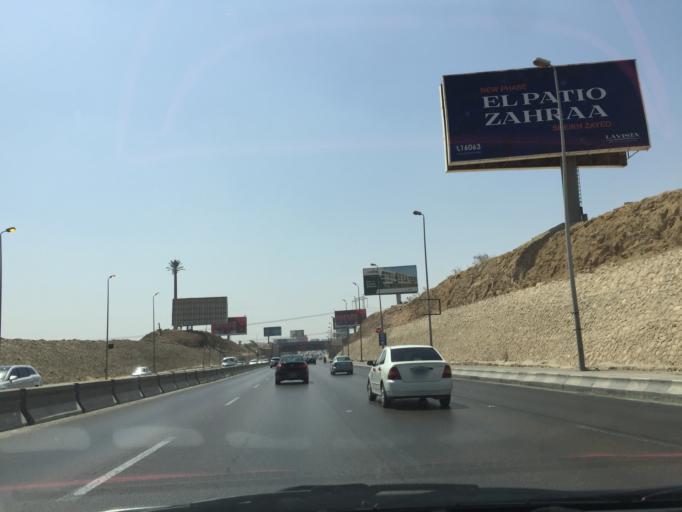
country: EG
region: Al Jizah
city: Awsim
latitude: 30.0573
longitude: 31.0781
